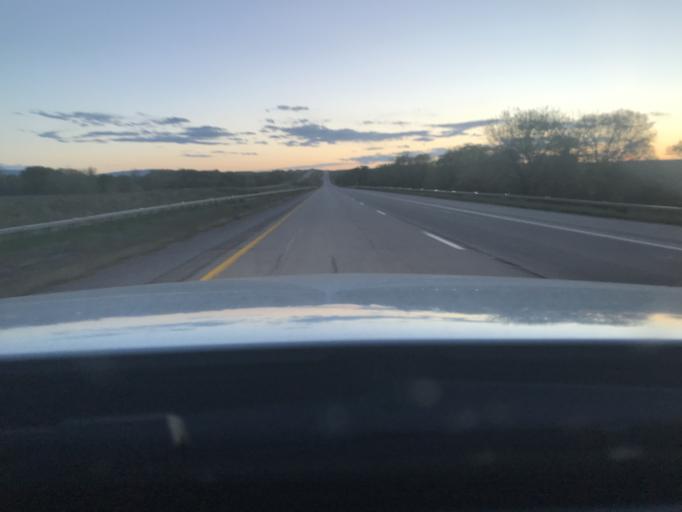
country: US
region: Wyoming
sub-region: Converse County
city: Glenrock
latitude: 42.8374
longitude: -105.8650
